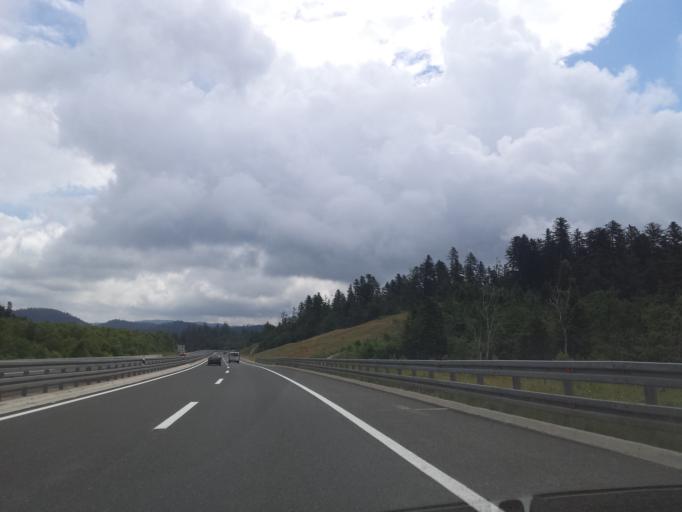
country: HR
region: Primorsko-Goranska
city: Hreljin
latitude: 45.3179
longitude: 14.6782
